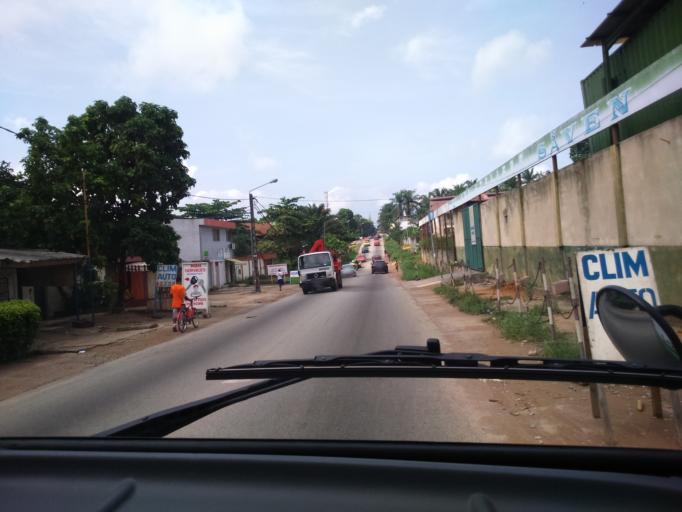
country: CI
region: Lagunes
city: Abidjan
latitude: 5.3607
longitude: -3.9787
